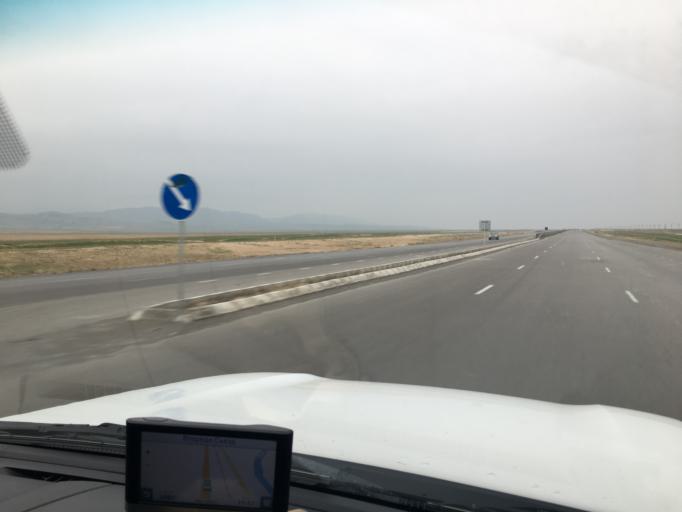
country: IR
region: Razavi Khorasan
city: Dargaz
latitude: 37.7430
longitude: 58.9724
